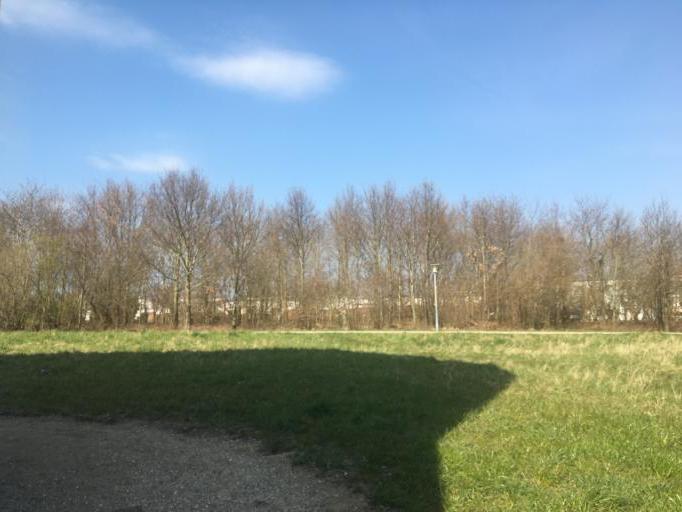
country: DK
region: Zealand
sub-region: Roskilde Kommune
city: Vindinge
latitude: 55.6528
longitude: 12.1271
